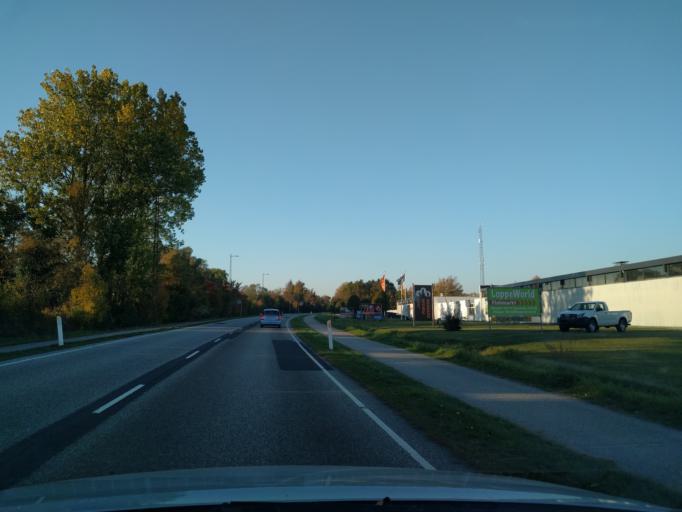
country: DK
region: Zealand
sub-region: Guldborgsund Kommune
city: Nykobing Falster
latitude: 54.7557
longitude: 11.8951
